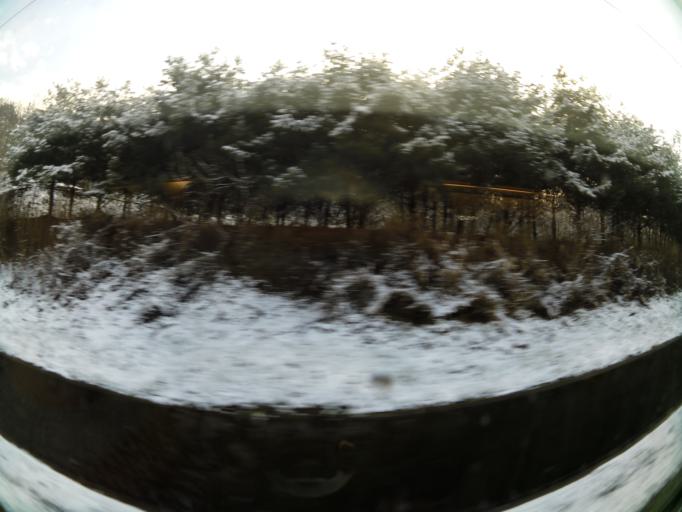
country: KR
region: Daejeon
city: Songgang-dong
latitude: 36.3816
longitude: 127.4181
